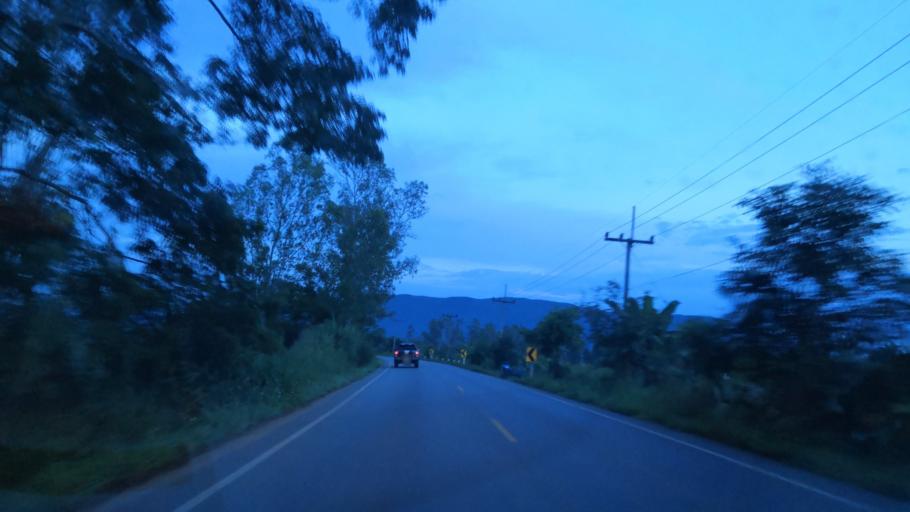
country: TH
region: Chiang Rai
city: Wiang Chiang Rung
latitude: 19.9654
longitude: 99.9883
